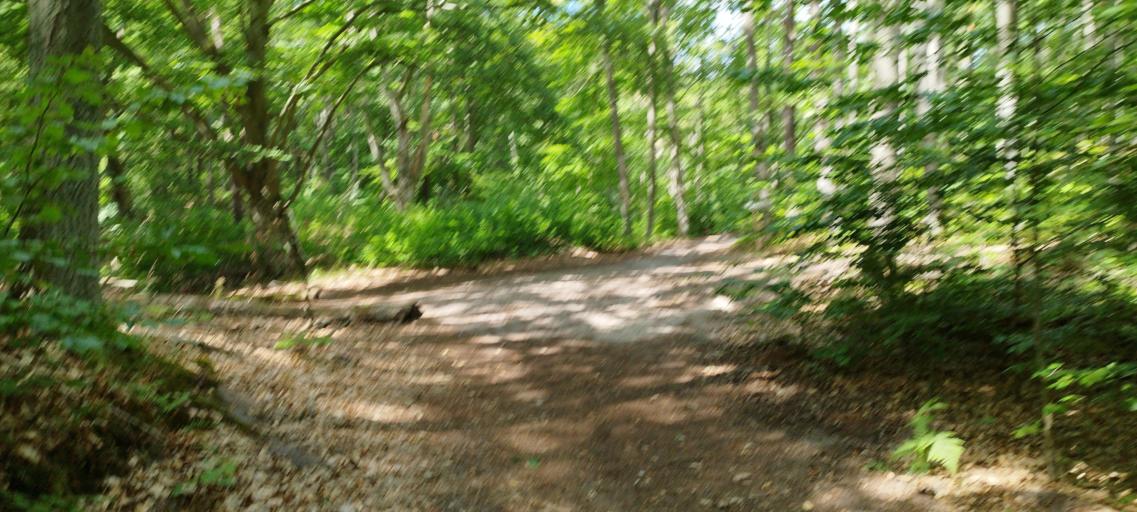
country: DE
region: Brandenburg
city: Mixdorf
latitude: 52.1552
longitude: 14.4453
